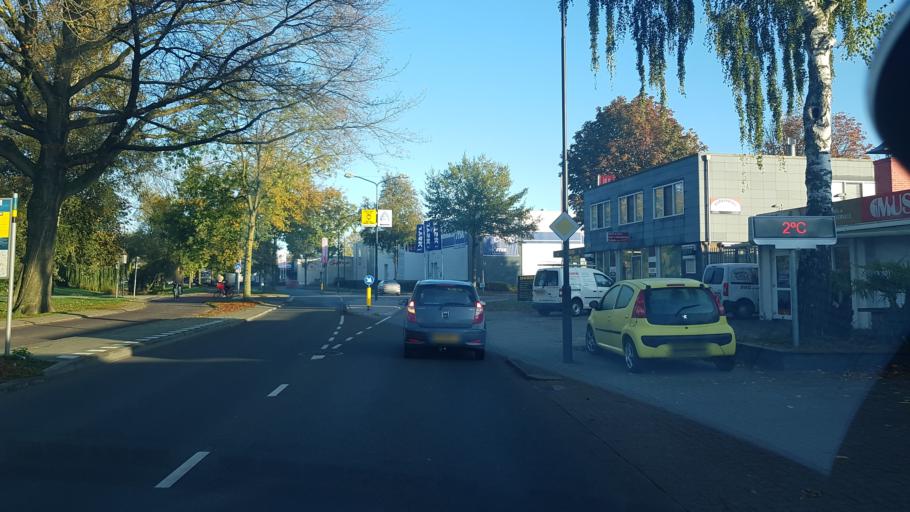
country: NL
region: Gelderland
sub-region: Gemeente Apeldoorn
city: Apeldoorn
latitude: 52.1993
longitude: 5.9799
